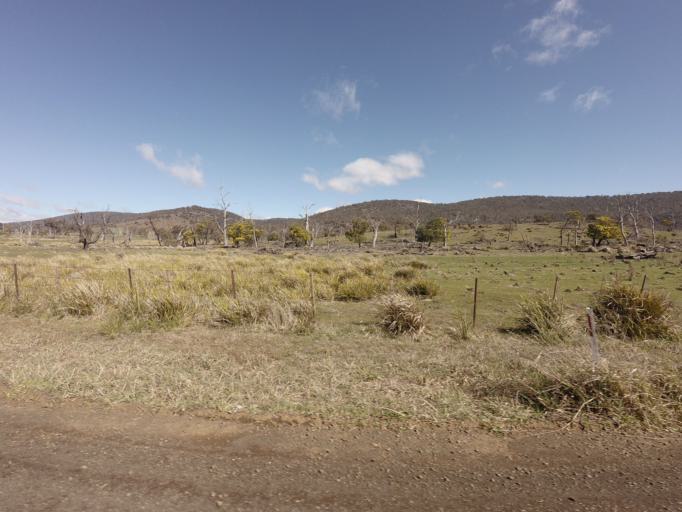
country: AU
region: Tasmania
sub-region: Northern Midlands
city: Evandale
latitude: -41.9417
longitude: 147.4266
